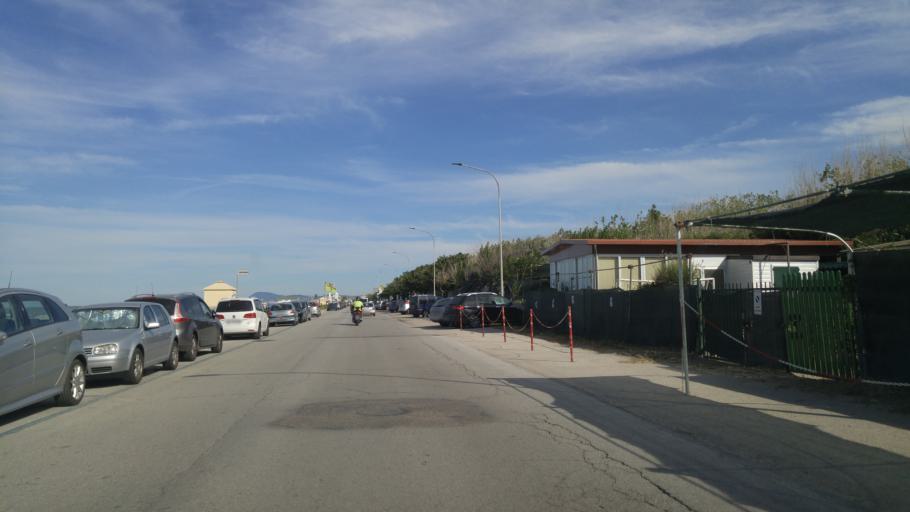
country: IT
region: The Marches
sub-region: Provincia di Ancona
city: Montignano-Marzocca
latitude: 43.6884
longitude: 13.2681
